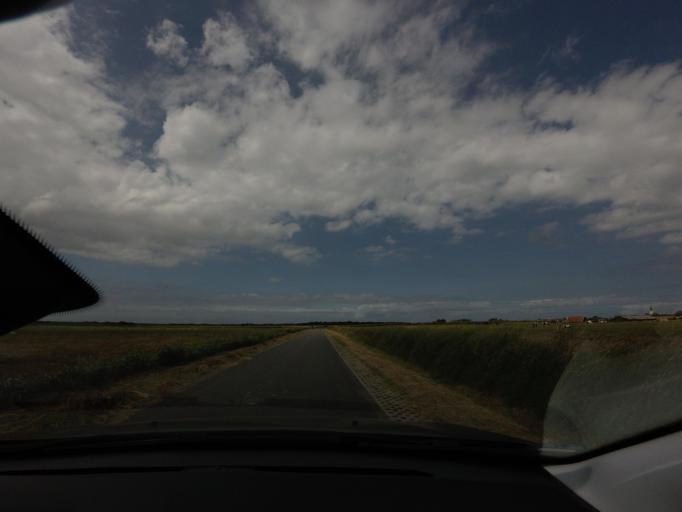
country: NL
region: North Holland
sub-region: Gemeente Texel
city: Den Burg
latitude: 53.0193
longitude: 4.7616
